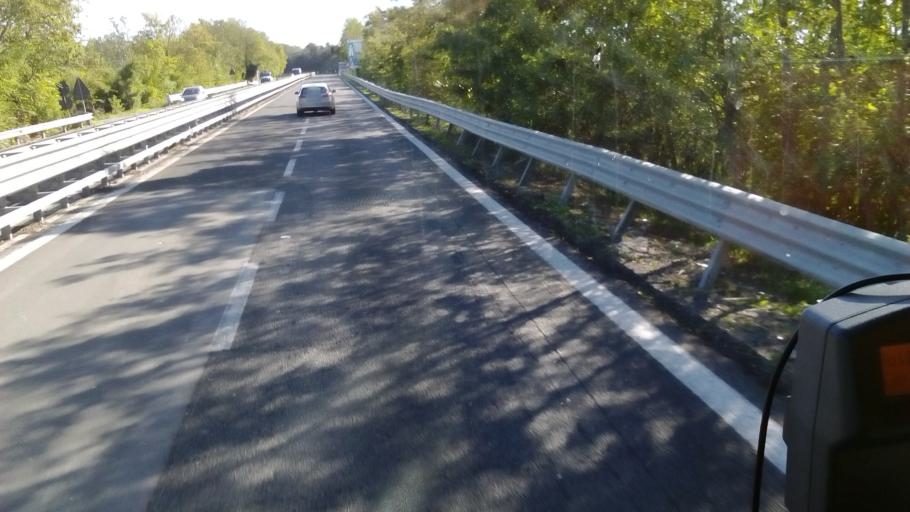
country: IT
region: Latium
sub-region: Provincia di Viterbo
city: Montalto di Castro
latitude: 42.3146
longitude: 11.6536
